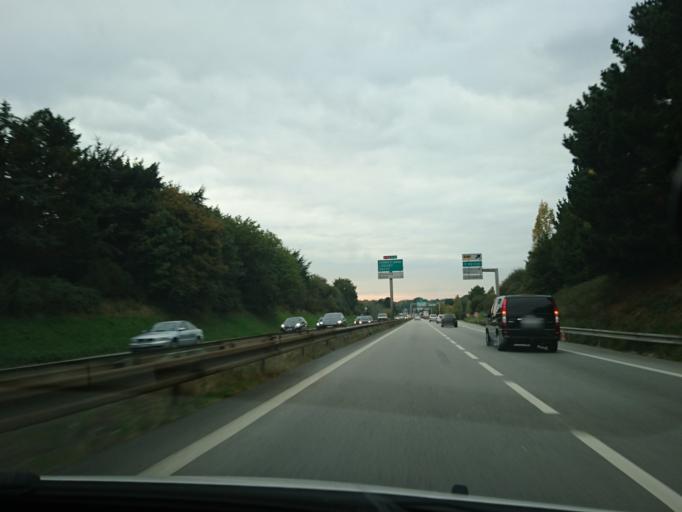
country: FR
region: Brittany
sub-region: Departement du Morbihan
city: Vannes
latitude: 47.6693
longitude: -2.7640
